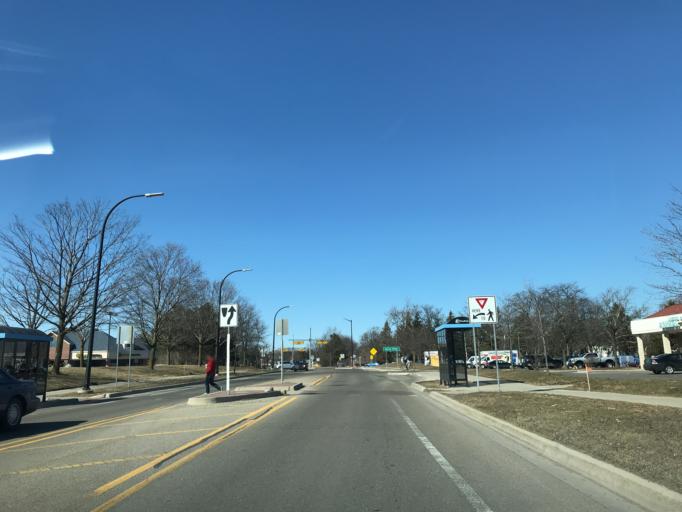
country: US
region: Michigan
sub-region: Washtenaw County
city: Ann Arbor
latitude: 42.3037
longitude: -83.7072
